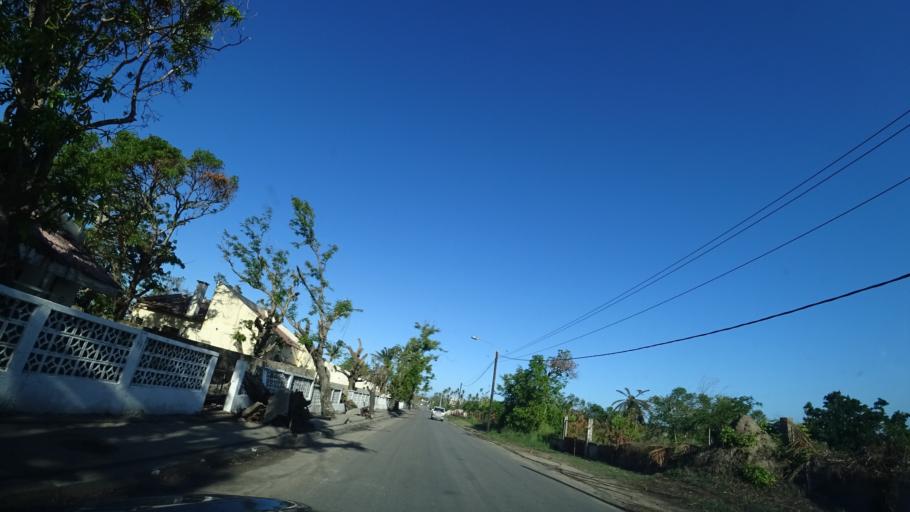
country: MZ
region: Sofala
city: Beira
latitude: -19.7994
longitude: 34.8969
